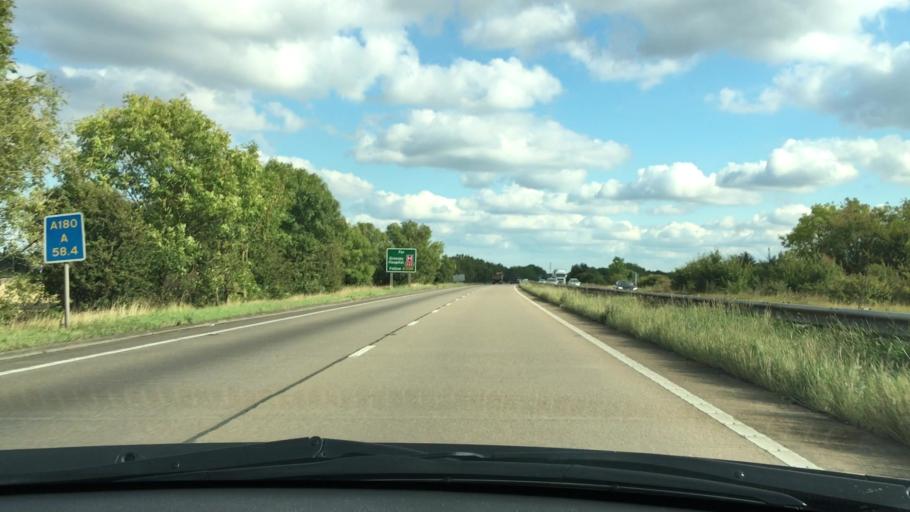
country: GB
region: England
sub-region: North East Lincolnshire
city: Healing
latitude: 53.5921
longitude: -0.1665
